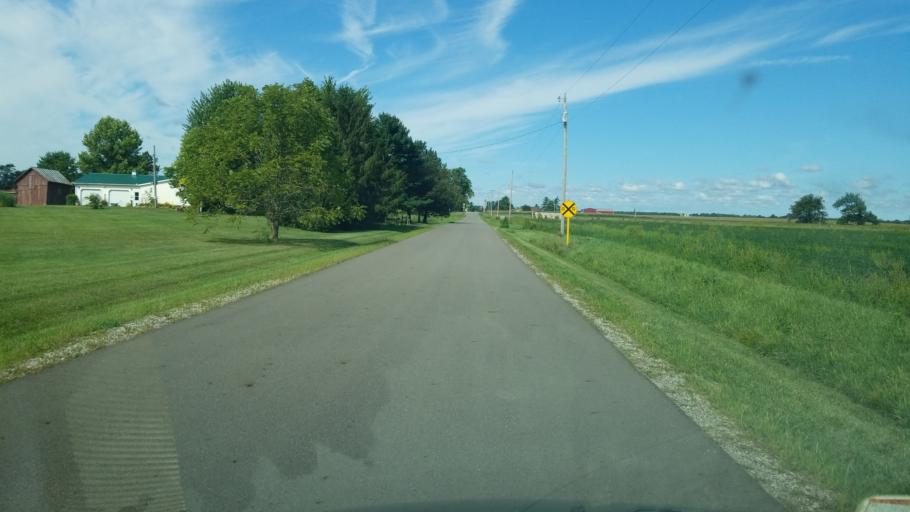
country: US
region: Ohio
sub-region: Delaware County
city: Ashley
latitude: 40.4379
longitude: -82.9323
